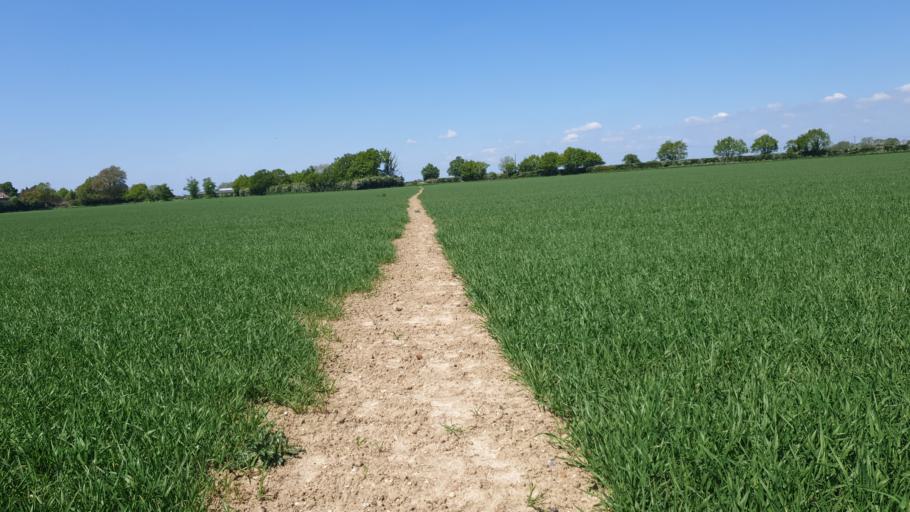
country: GB
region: England
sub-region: Essex
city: Manningtree
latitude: 51.9093
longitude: 1.0506
